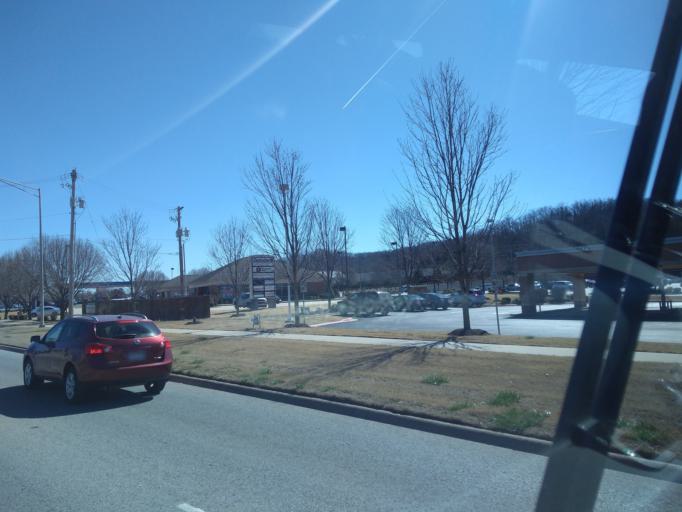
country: US
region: Arkansas
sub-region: Washington County
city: Farmington
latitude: 36.0514
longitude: -94.2046
